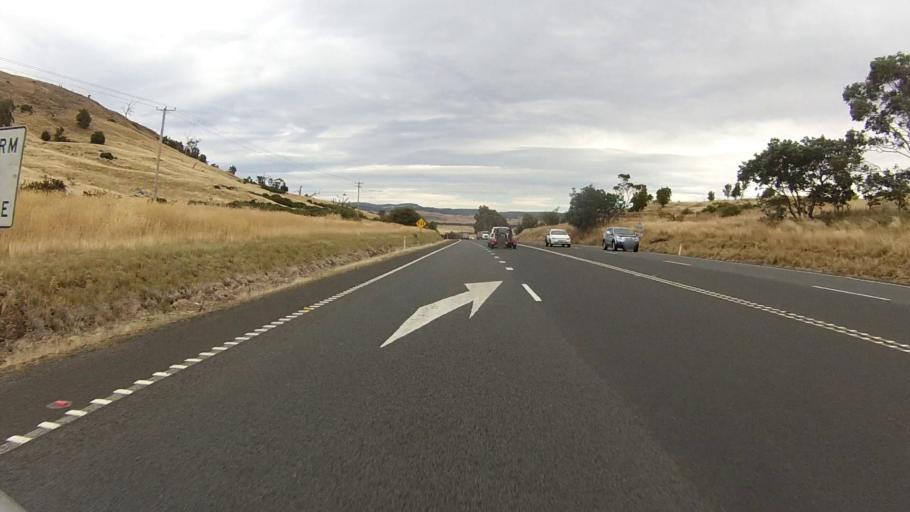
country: AU
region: Tasmania
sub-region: Brighton
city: Bridgewater
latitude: -42.3339
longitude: 147.3435
